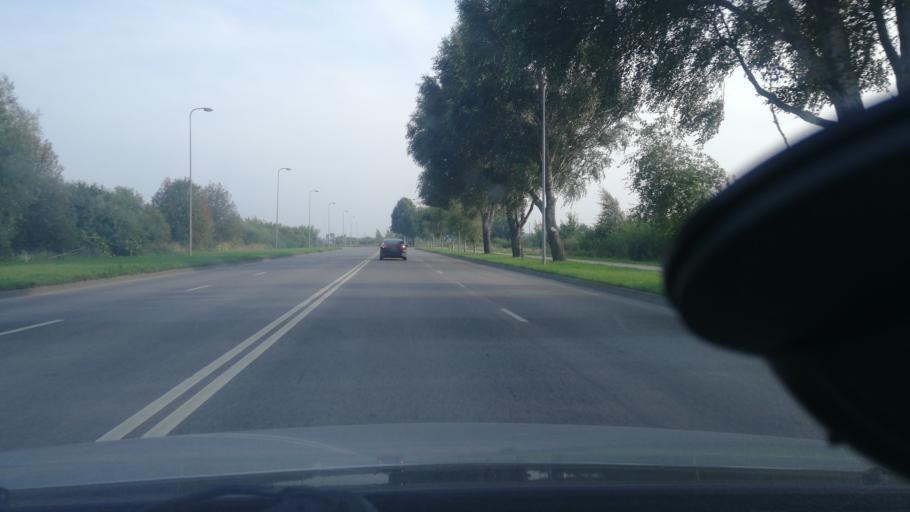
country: LT
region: Klaipedos apskritis
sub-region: Klaipeda
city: Klaipeda
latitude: 55.6572
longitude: 21.1702
